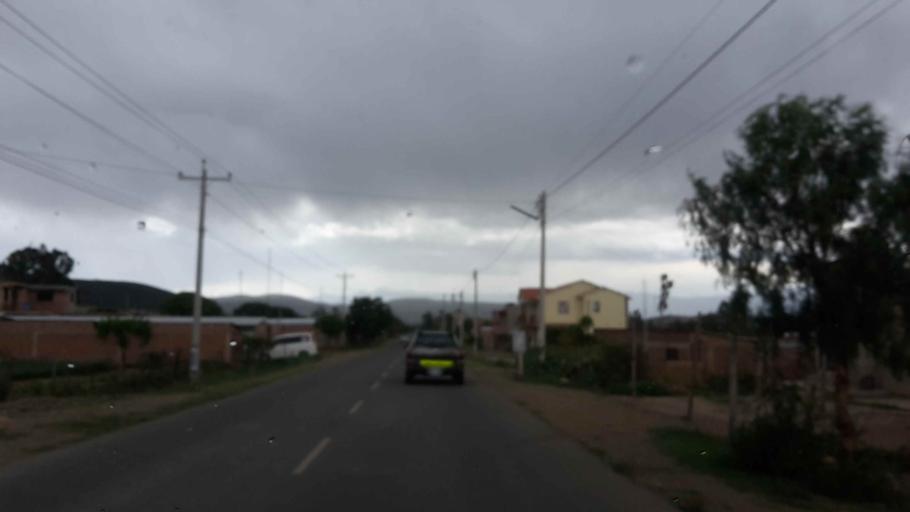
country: BO
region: Cochabamba
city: Tarata
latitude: -17.5910
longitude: -66.0454
